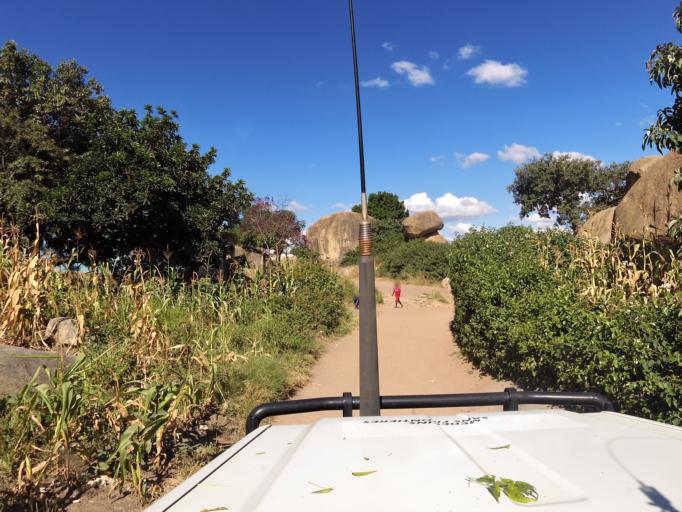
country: ZW
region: Harare
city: Epworth
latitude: -17.8797
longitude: 31.1371
